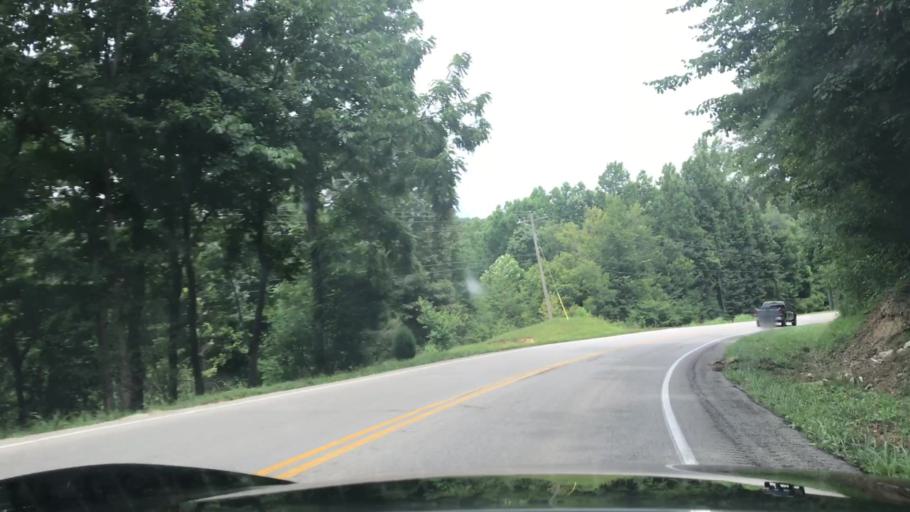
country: US
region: Kentucky
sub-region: Butler County
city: Morgantown
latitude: 37.2097
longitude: -86.7229
